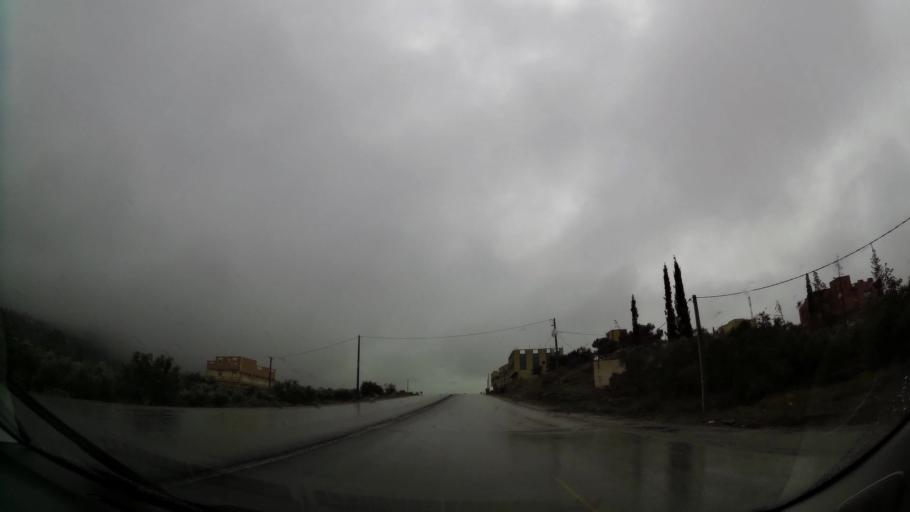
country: MA
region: Taza-Al Hoceima-Taounate
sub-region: Taza
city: Aknoul
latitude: 34.8058
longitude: -3.7374
